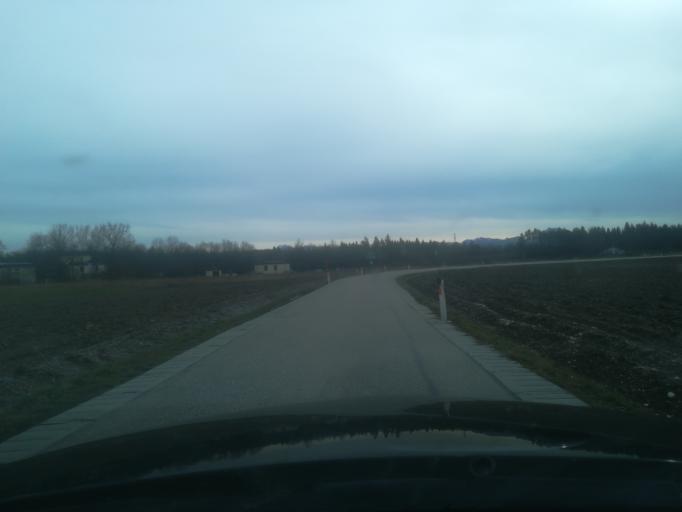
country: AT
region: Upper Austria
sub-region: Wels-Land
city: Bad Wimsbach-Neydharting
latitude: 48.0966
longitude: 13.9211
